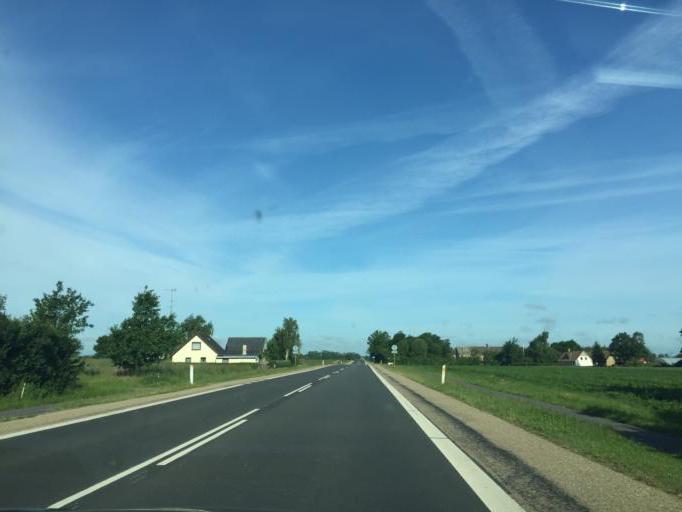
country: DK
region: South Denmark
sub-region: Middelfart Kommune
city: Norre Aby
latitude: 55.4749
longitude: 9.8697
